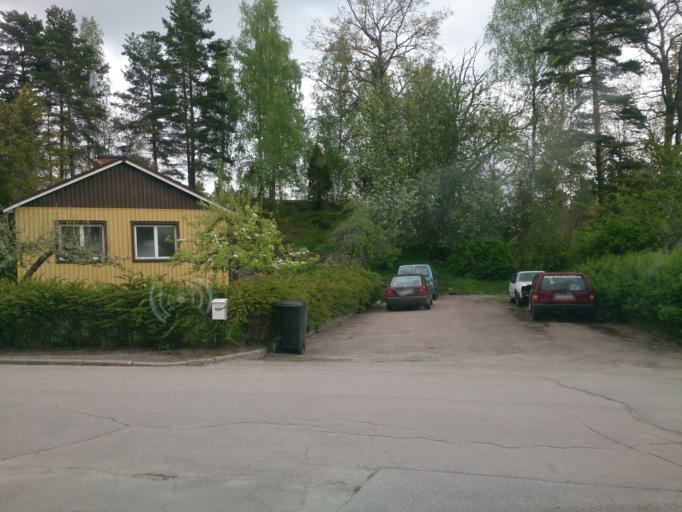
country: SE
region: OEstergoetland
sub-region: Atvidabergs Kommun
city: Atvidaberg
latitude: 58.2110
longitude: 16.0055
